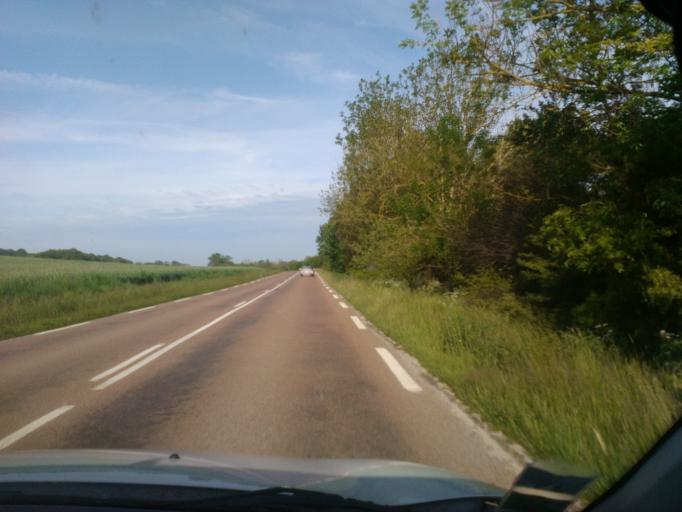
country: FR
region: Champagne-Ardenne
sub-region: Departement de l'Aube
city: Vendeuvre-sur-Barse
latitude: 48.2369
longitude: 4.4263
